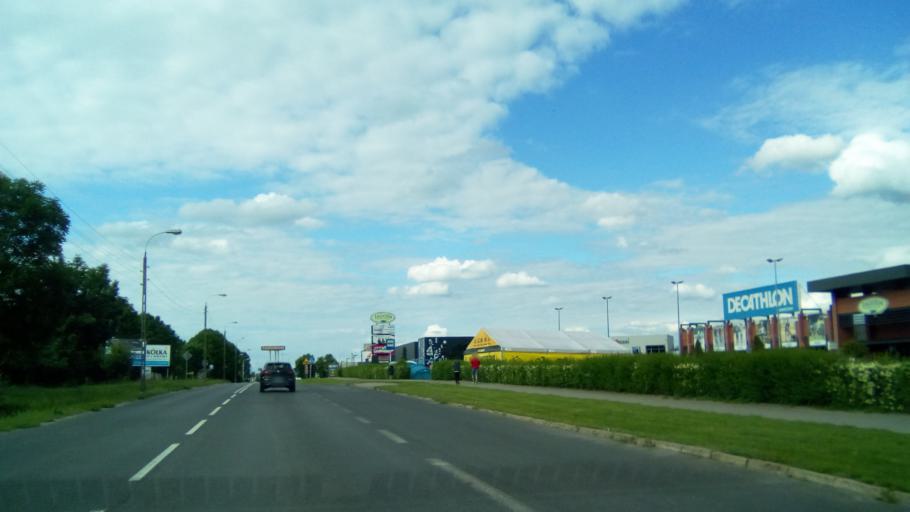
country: PL
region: Greater Poland Voivodeship
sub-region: Powiat gnieznienski
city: Gniezno
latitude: 52.5589
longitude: 17.6082
